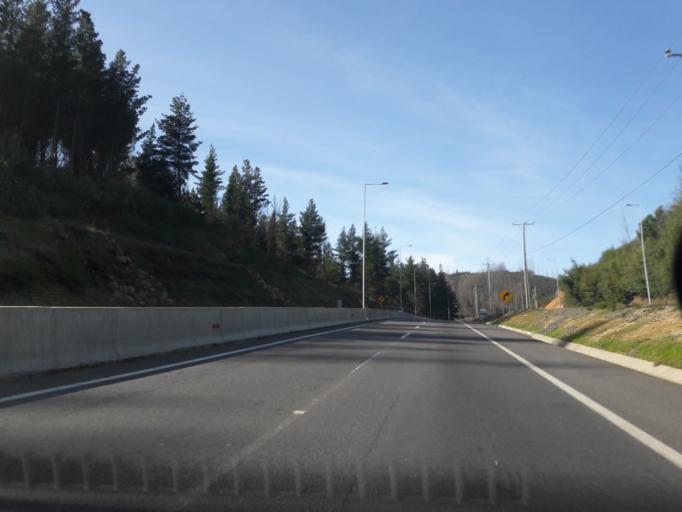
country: CL
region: Biobio
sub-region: Provincia de Concepcion
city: Penco
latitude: -36.8572
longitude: -72.8645
